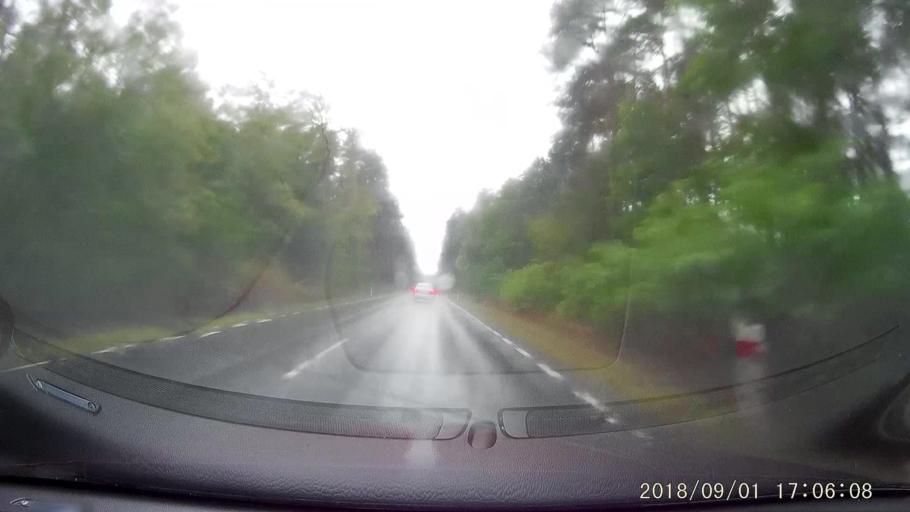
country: PL
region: Lubusz
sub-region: Powiat zielonogorski
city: Swidnica
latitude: 51.8464
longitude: 15.3411
